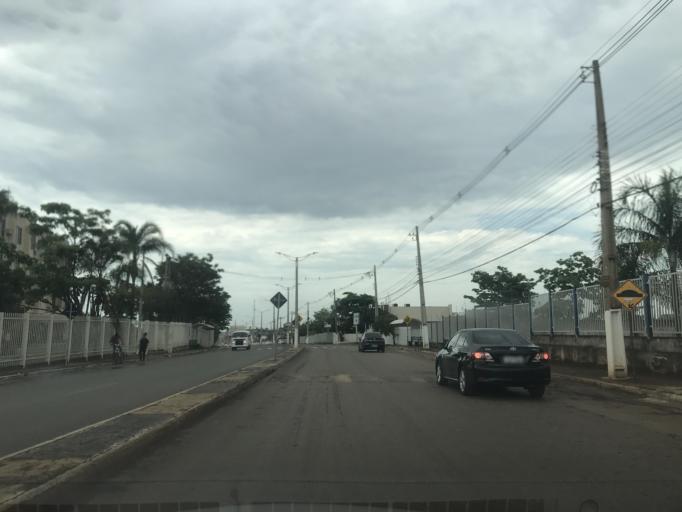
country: BR
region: Goias
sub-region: Luziania
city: Luziania
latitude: -16.2269
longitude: -47.9382
